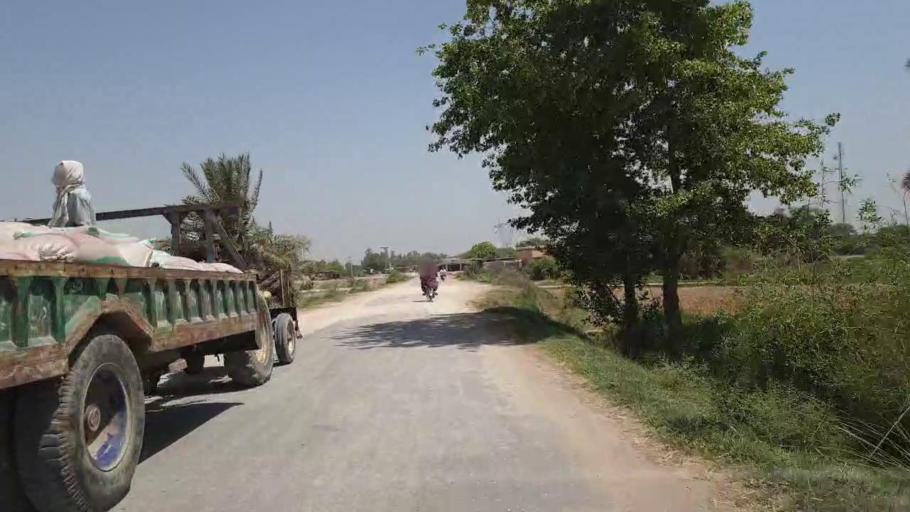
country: PK
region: Sindh
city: Adilpur
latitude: 27.8903
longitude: 69.2890
